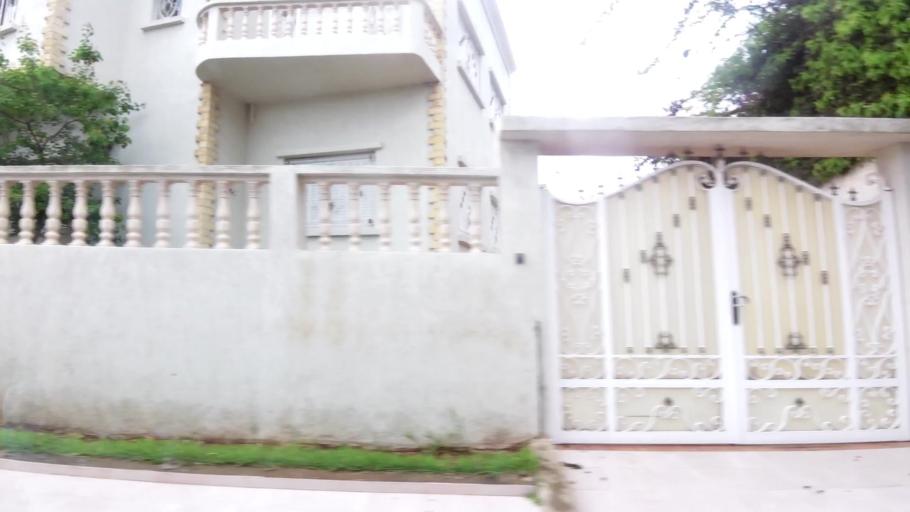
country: MA
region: Grand Casablanca
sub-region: Nouaceur
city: Bouskoura
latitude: 33.5176
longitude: -7.6425
